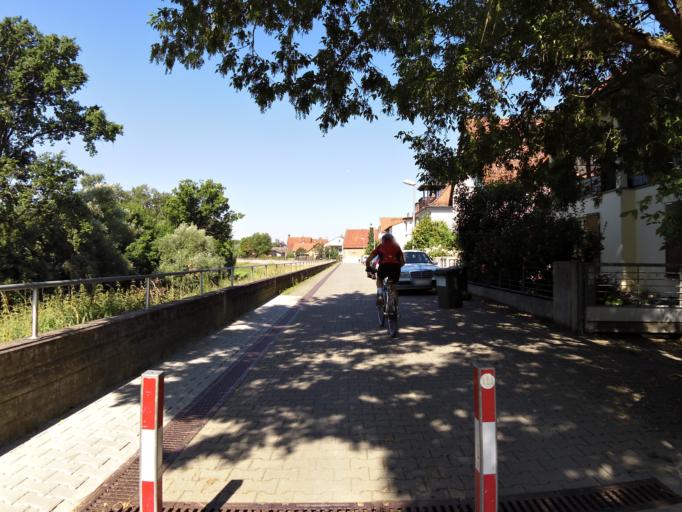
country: DE
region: Hesse
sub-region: Regierungsbezirk Darmstadt
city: Ginsheim-Gustavsburg
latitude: 49.9616
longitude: 8.3503
